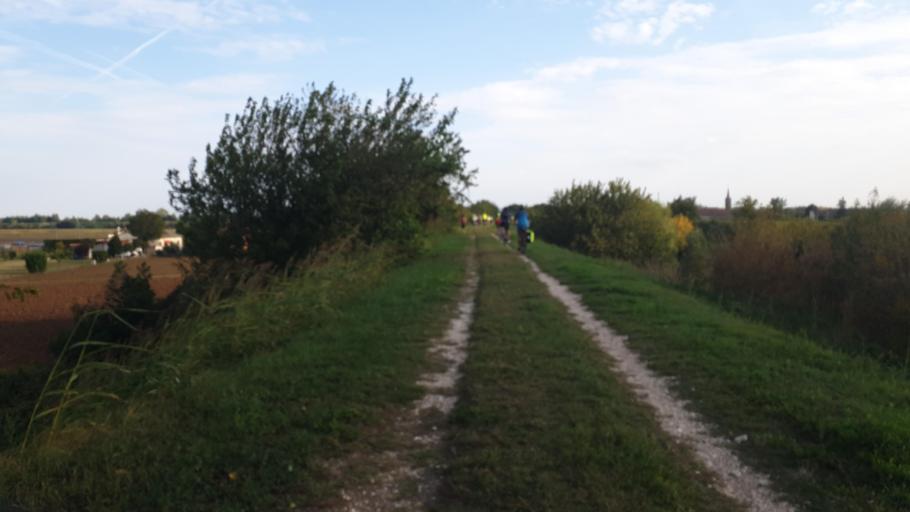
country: IT
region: Veneto
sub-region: Provincia di Padova
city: Montagnana
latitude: 45.2546
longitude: 11.4782
